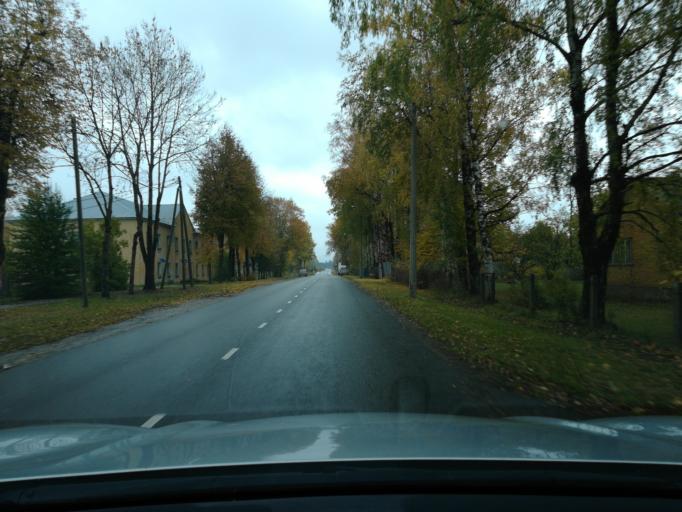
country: EE
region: Ida-Virumaa
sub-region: Johvi vald
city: Johvi
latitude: 59.3098
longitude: 27.4558
